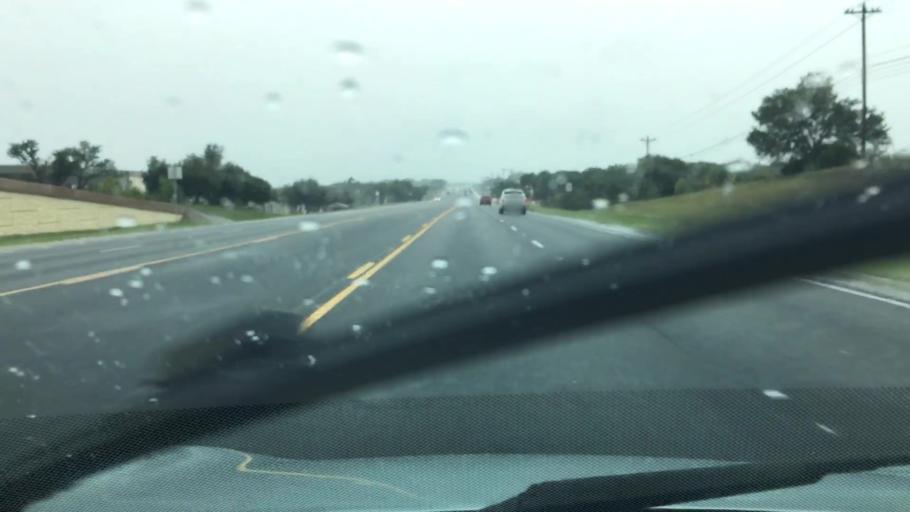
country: US
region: Texas
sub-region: Hays County
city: Dripping Springs
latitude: 30.2058
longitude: -97.9802
